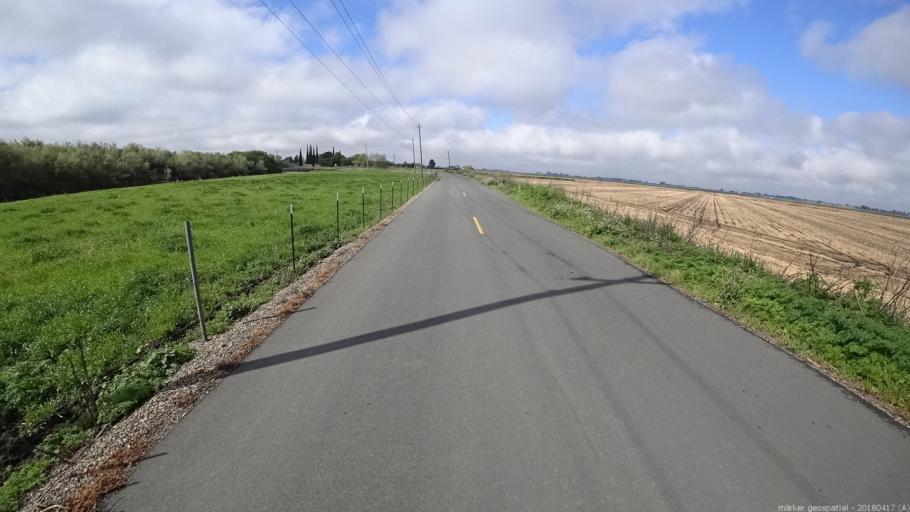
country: US
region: California
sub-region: Sacramento County
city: Walnut Grove
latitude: 38.2459
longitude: -121.5631
